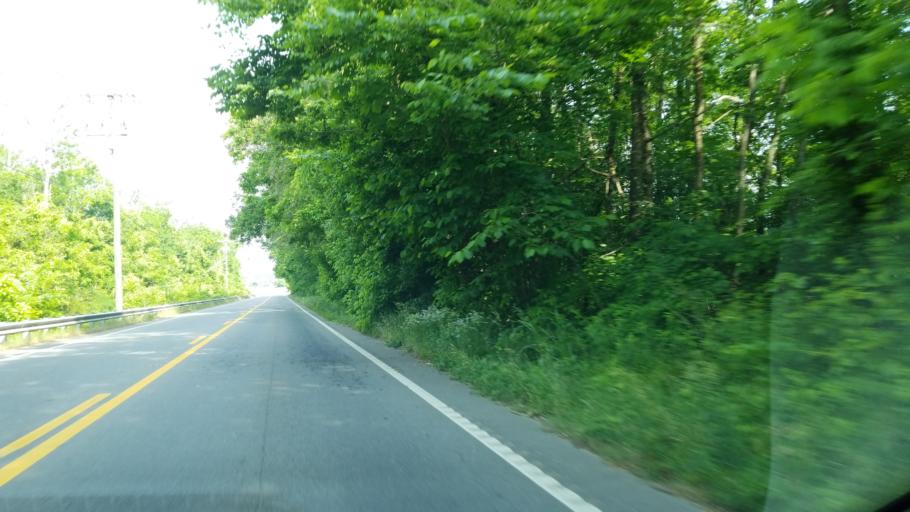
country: US
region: Tennessee
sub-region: Hamilton County
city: Collegedale
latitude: 35.0784
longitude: -85.0476
